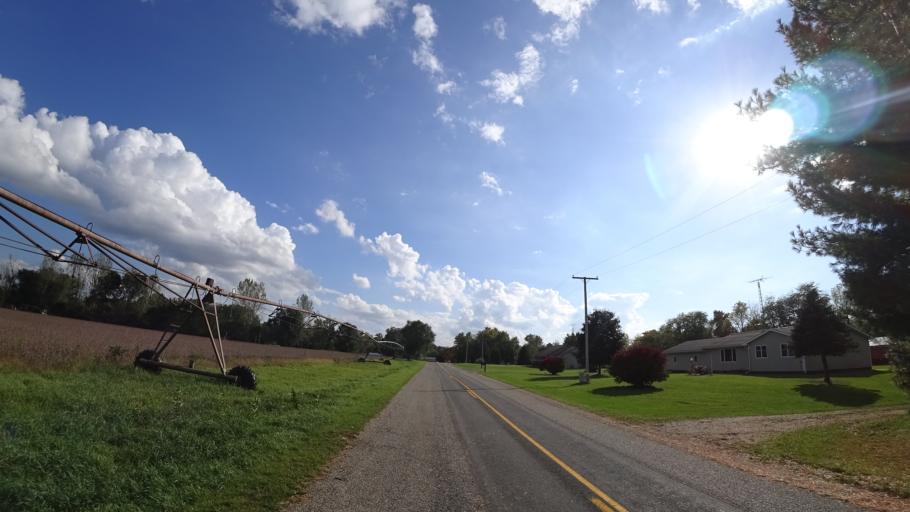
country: US
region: Michigan
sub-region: Saint Joseph County
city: Three Rivers
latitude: 41.9443
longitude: -85.6042
